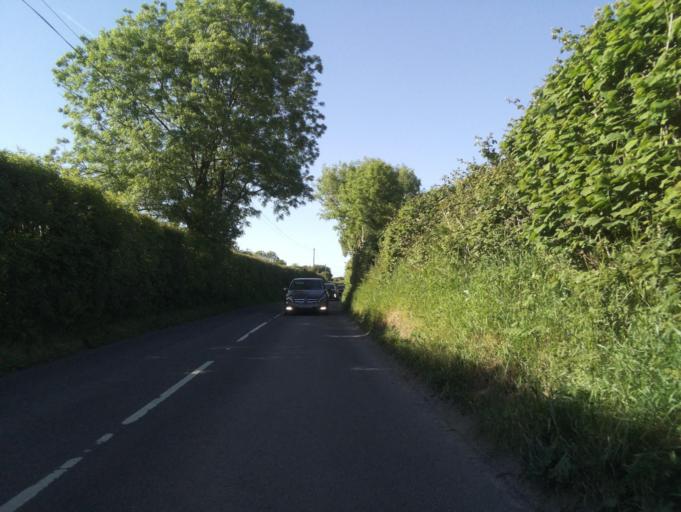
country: GB
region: England
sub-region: Somerset
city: Crewkerne
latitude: 50.8142
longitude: -2.8580
